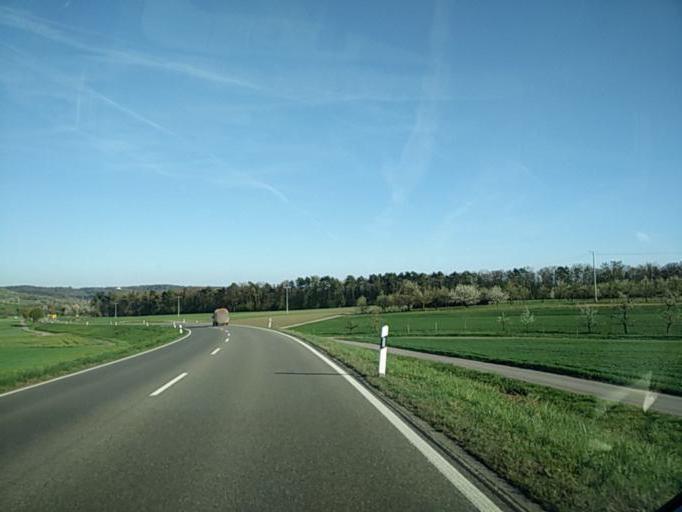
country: DE
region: Baden-Wuerttemberg
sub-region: Regierungsbezirk Stuttgart
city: Hildrizhausen
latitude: 48.5695
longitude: 8.9368
